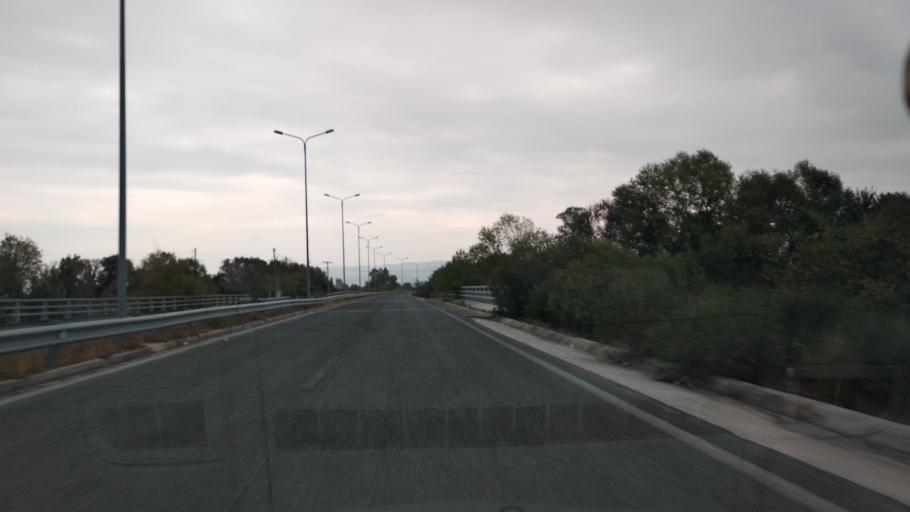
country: GR
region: Thessaly
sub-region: Trikala
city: Pyrgetos
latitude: 39.5689
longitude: 21.7407
